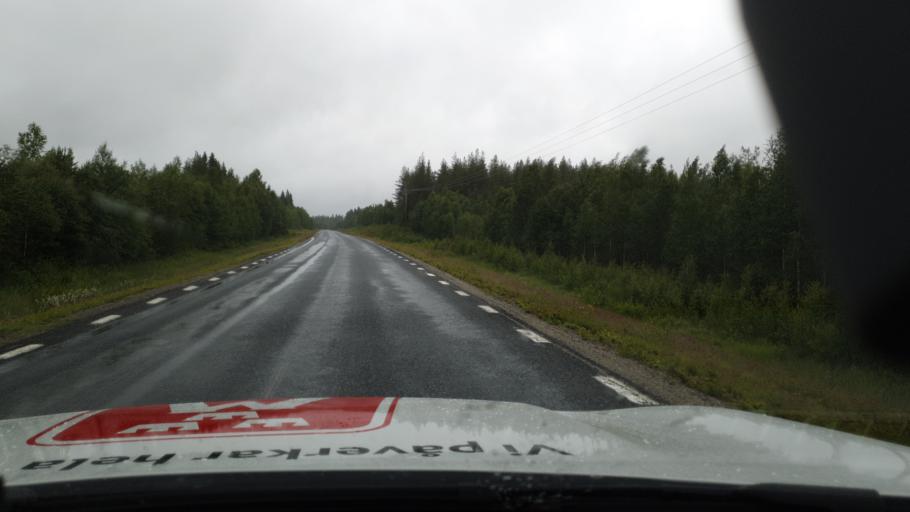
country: SE
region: Vaesterbotten
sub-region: Lycksele Kommun
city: Soderfors
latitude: 64.4724
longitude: 18.2122
